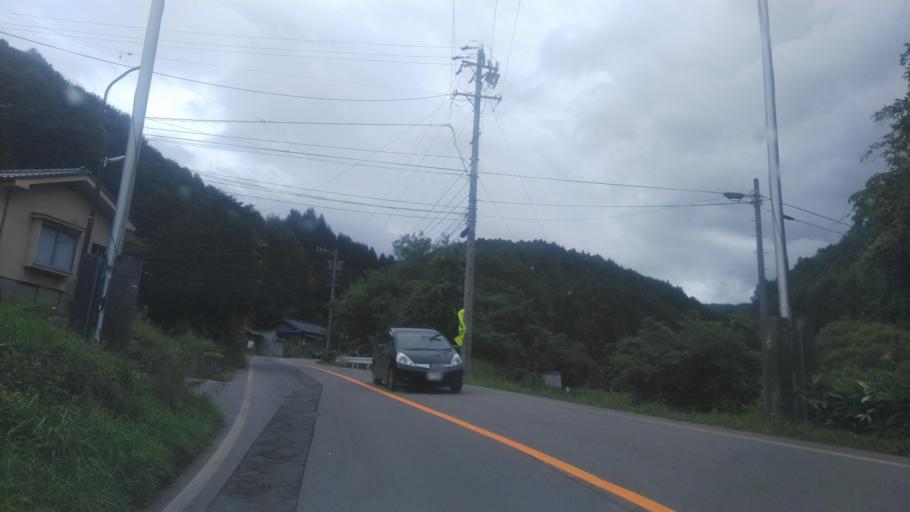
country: JP
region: Nagano
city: Ueda
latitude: 36.4885
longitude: 138.3741
